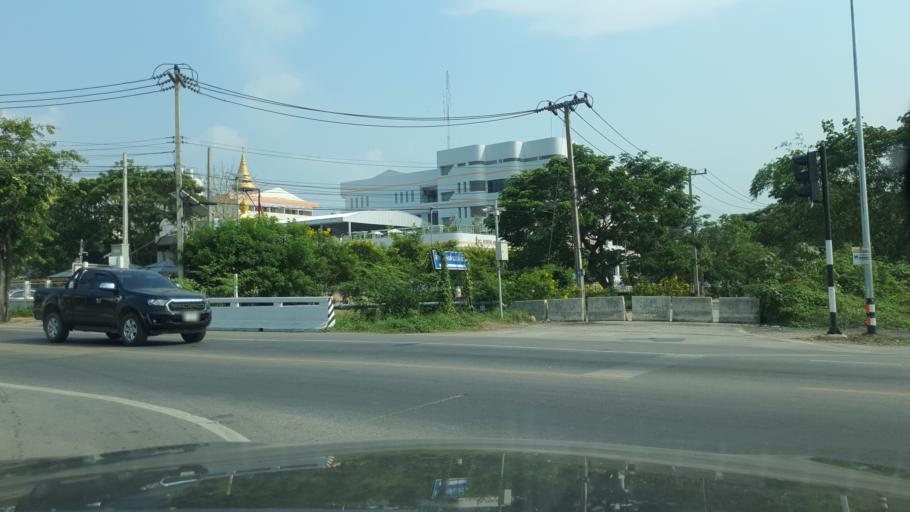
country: TH
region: Lamphun
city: Lamphun
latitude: 18.5839
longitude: 98.9934
